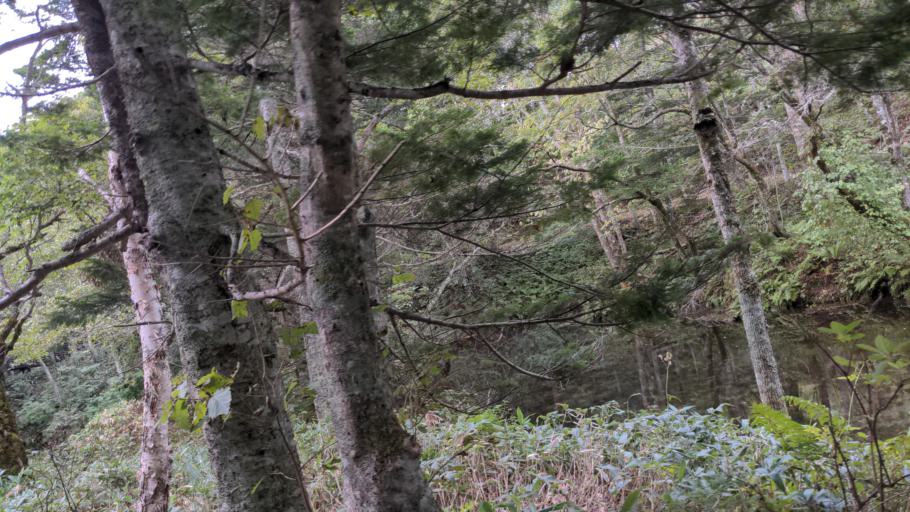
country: JP
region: Hokkaido
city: Abashiri
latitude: 43.6454
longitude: 144.5499
